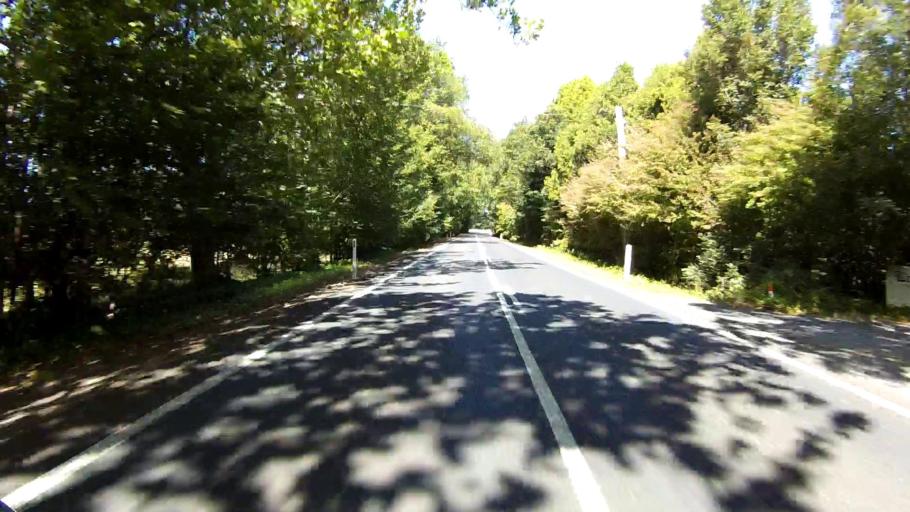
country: AU
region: Tasmania
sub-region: Break O'Day
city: St Helens
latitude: -42.0629
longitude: 148.0628
